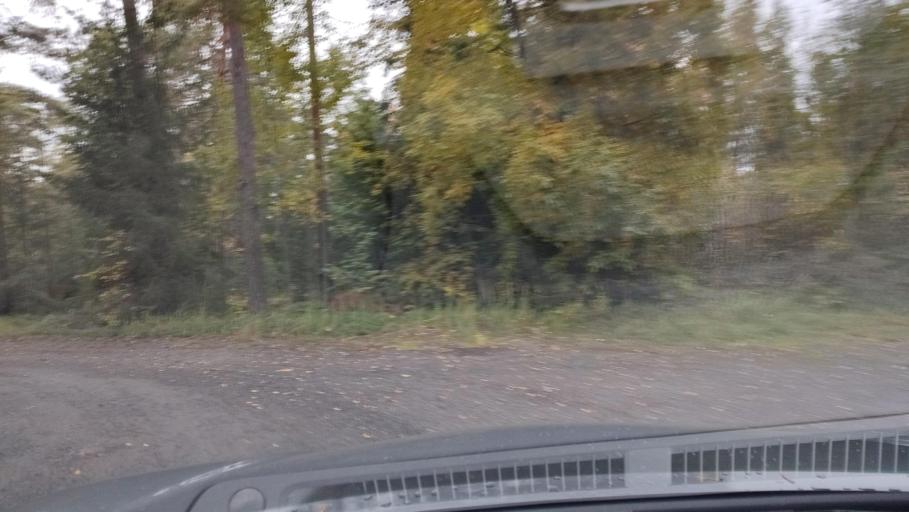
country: FI
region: Ostrobothnia
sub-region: Sydosterbotten
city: Kristinestad
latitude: 62.2750
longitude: 21.4053
